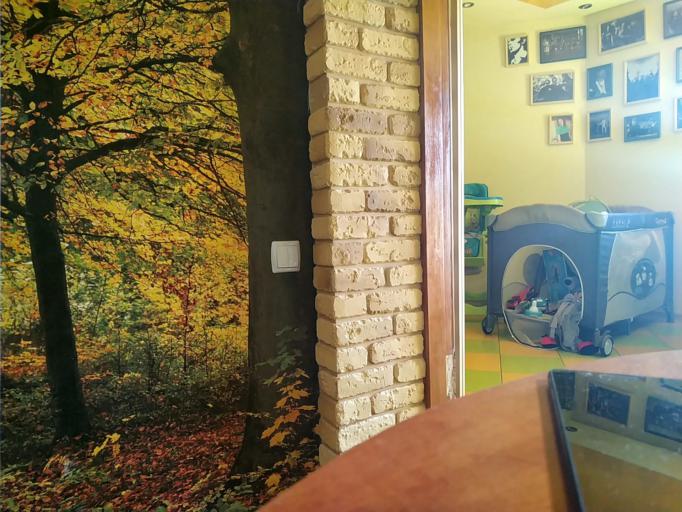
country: RU
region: Tverskaya
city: Vydropuzhsk
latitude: 57.4614
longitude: 34.7131
